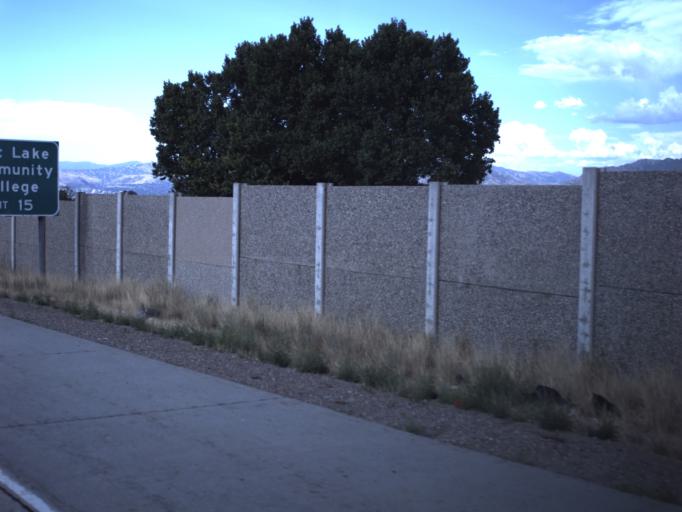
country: US
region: Utah
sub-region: Salt Lake County
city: Taylorsville
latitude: 40.6550
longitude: -111.9524
